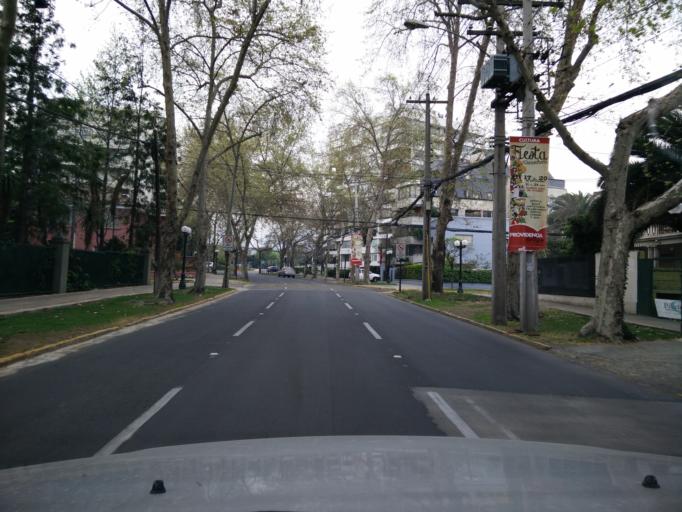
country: CL
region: Santiago Metropolitan
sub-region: Provincia de Santiago
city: Villa Presidente Frei, Nunoa, Santiago, Chile
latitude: -33.4251
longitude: -70.5946
